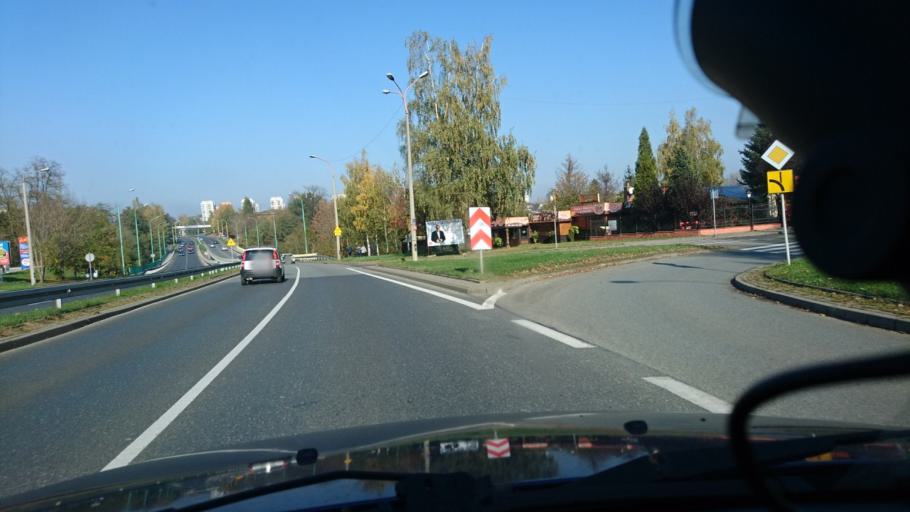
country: PL
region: Silesian Voivodeship
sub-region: Bielsko-Biala
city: Bielsko-Biala
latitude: 49.8052
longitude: 19.0307
